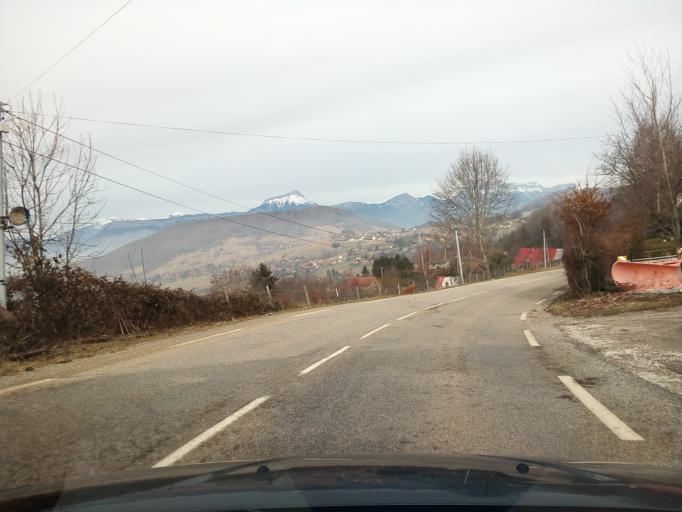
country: FR
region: Rhone-Alpes
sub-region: Departement de l'Isere
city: Revel
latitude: 45.1424
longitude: 5.8549
